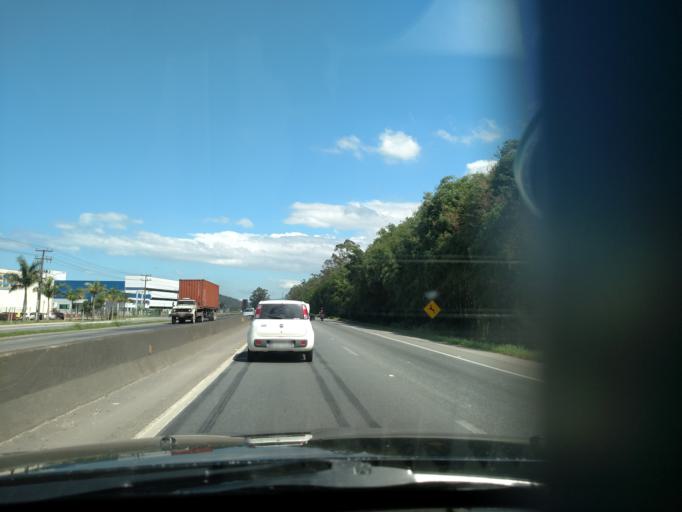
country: BR
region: Santa Catarina
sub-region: Itajai
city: Itajai
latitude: -26.9255
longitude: -48.7066
